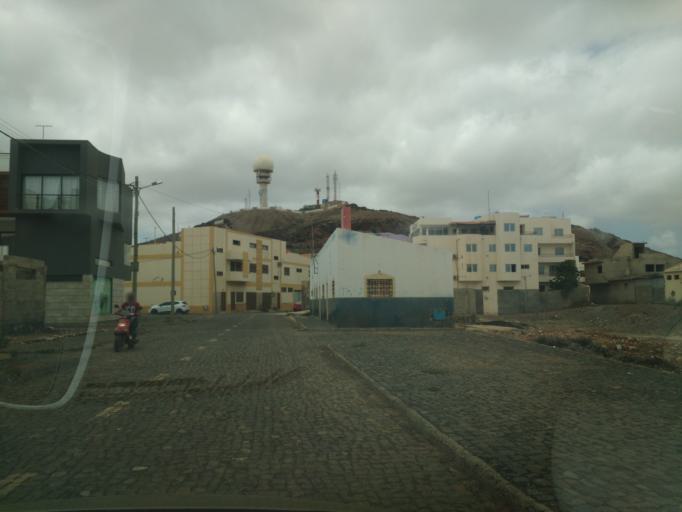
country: CV
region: Sal
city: Espargos
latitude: 16.7543
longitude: -22.9411
